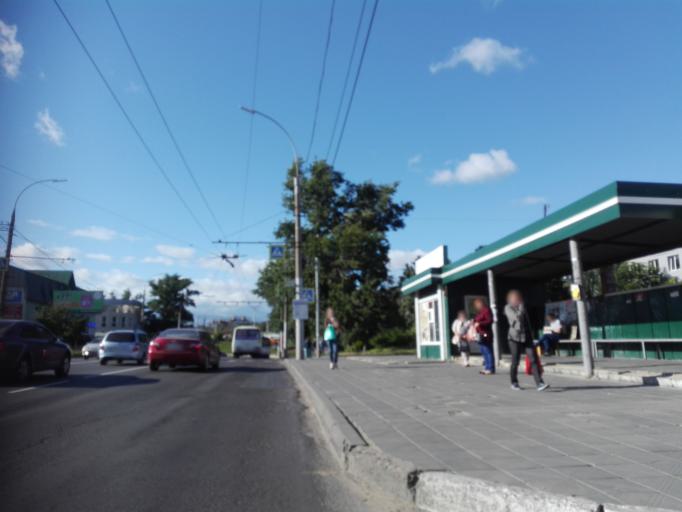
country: RU
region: Orjol
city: Orel
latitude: 52.9824
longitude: 36.1073
